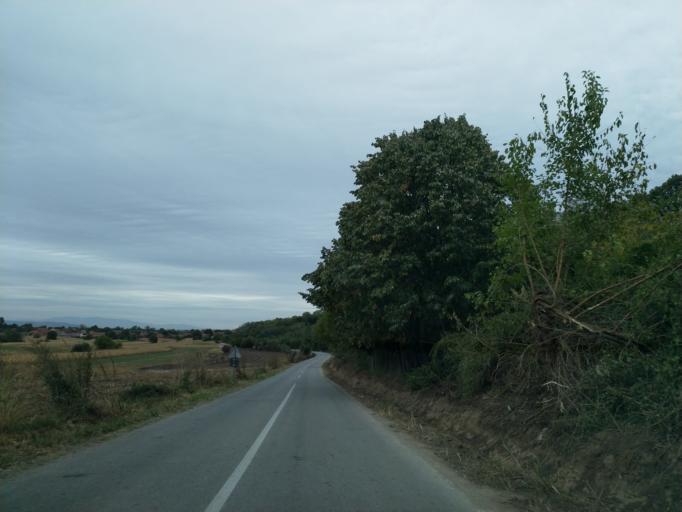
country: RS
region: Central Serbia
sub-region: Pomoravski Okrug
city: Paracin
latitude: 43.8509
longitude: 21.3227
